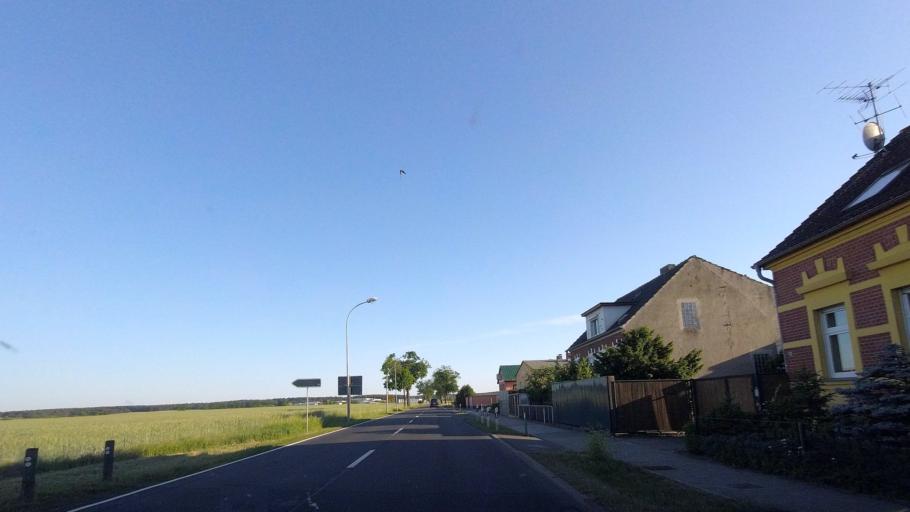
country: DE
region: Brandenburg
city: Brandenburg an der Havel
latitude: 52.3879
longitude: 12.5941
